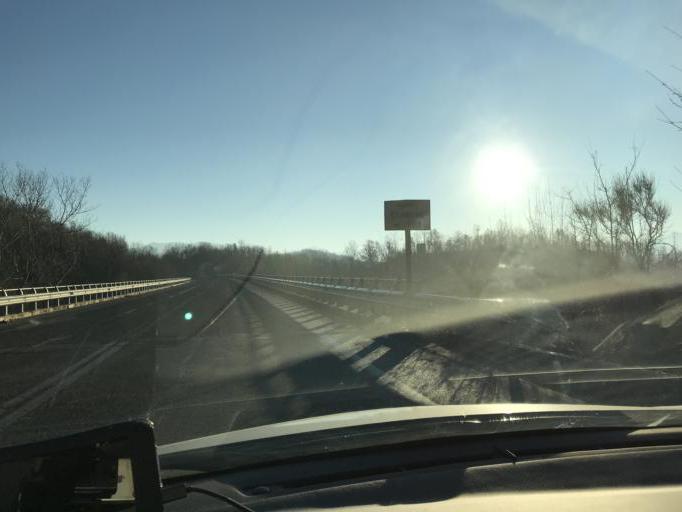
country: IT
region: Latium
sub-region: Provincia di Rieti
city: Fiamignano
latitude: 42.2613
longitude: 13.0935
